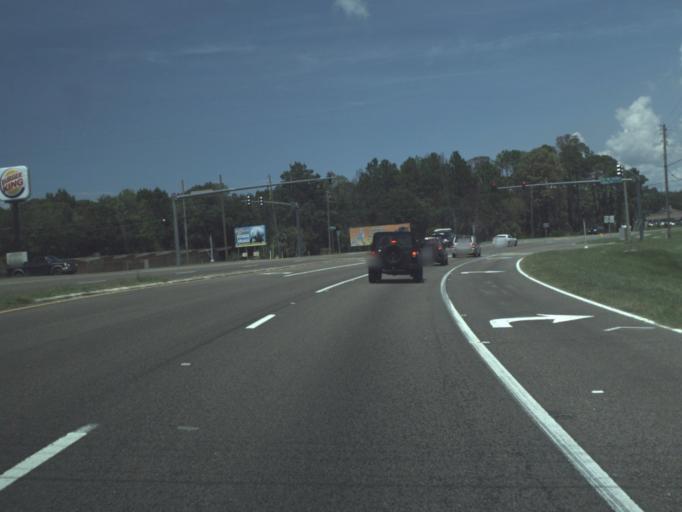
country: US
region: Florida
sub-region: Citrus County
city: Homosassa Springs
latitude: 28.7973
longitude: -82.5756
